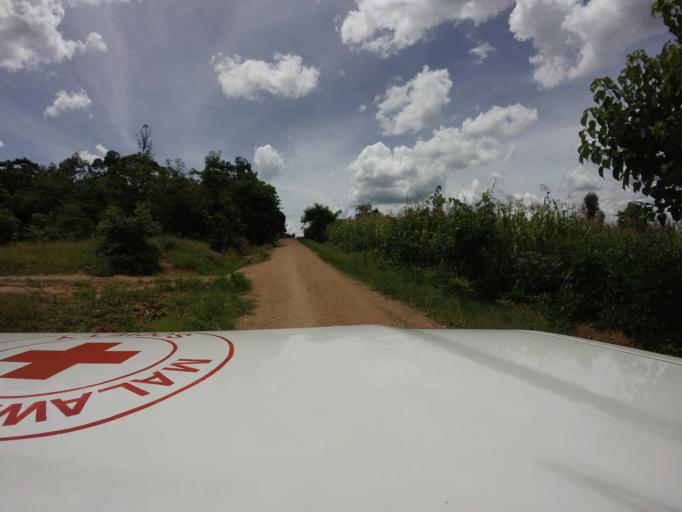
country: MW
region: Southern Region
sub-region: Thyolo District
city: Thyolo
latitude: -15.9540
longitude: 35.1653
